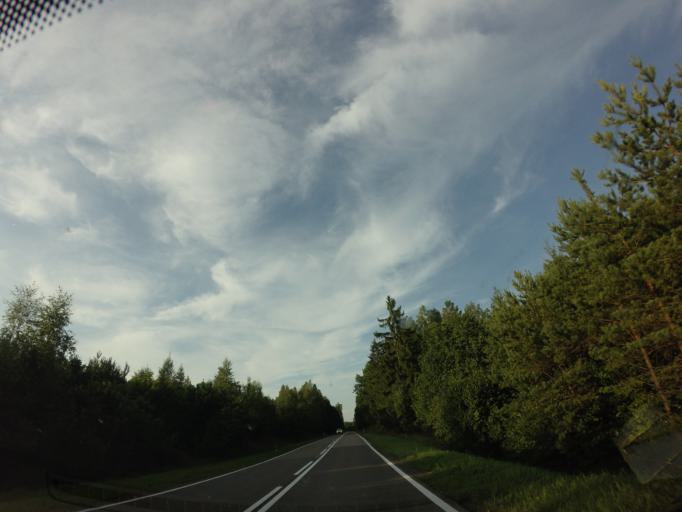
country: PL
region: Podlasie
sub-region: Powiat sejnenski
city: Sejny
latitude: 54.0058
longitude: 23.3212
